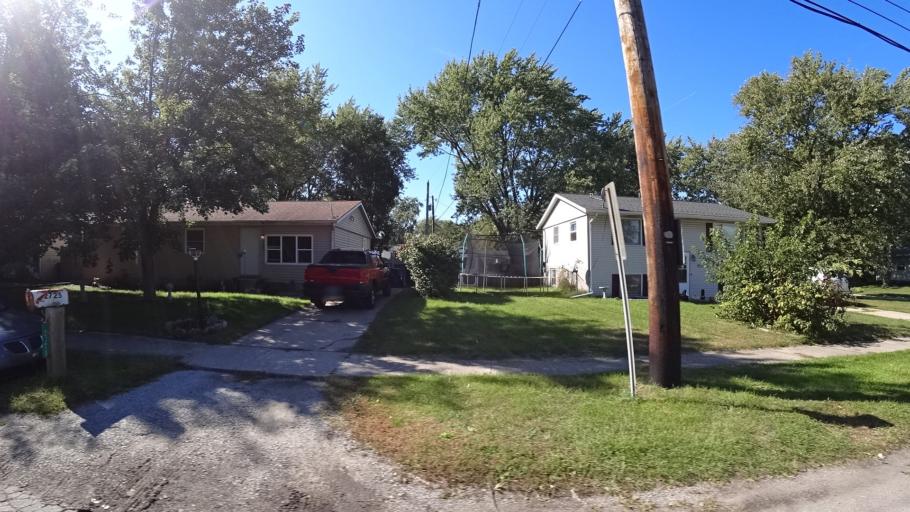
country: US
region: Indiana
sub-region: LaPorte County
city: Michigan City
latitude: 41.6916
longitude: -86.9035
